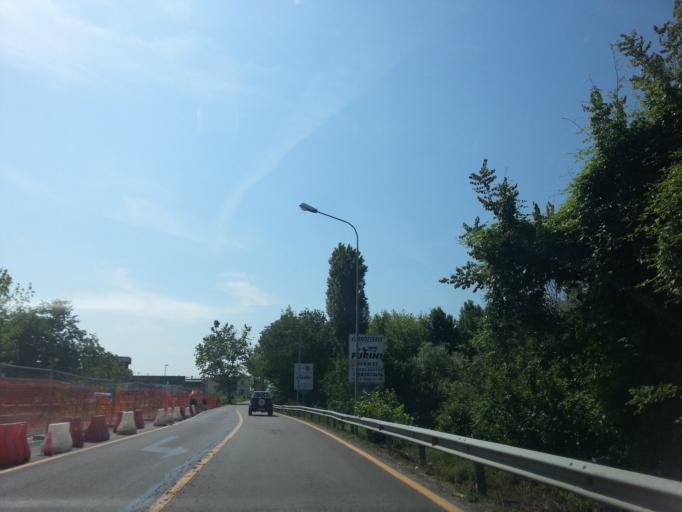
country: IT
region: Emilia-Romagna
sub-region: Provincia di Reggio Emilia
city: Pratissolo
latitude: 44.6250
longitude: 10.6678
